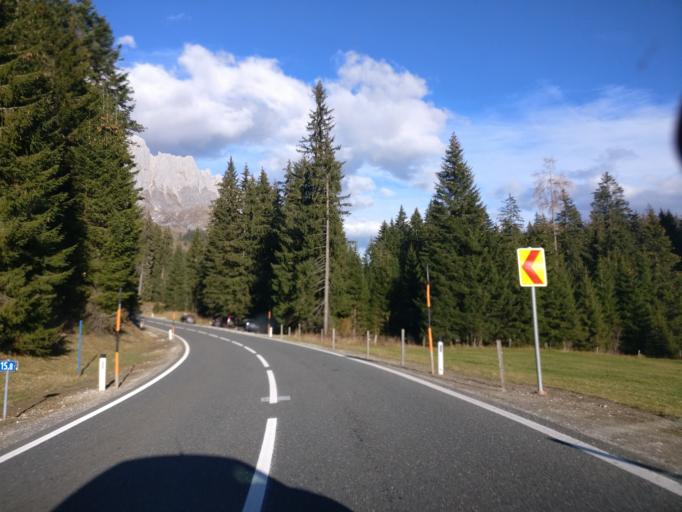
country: AT
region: Salzburg
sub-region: Politischer Bezirk Zell am See
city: Dienten am Hochkonig
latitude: 47.3907
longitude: 13.0654
